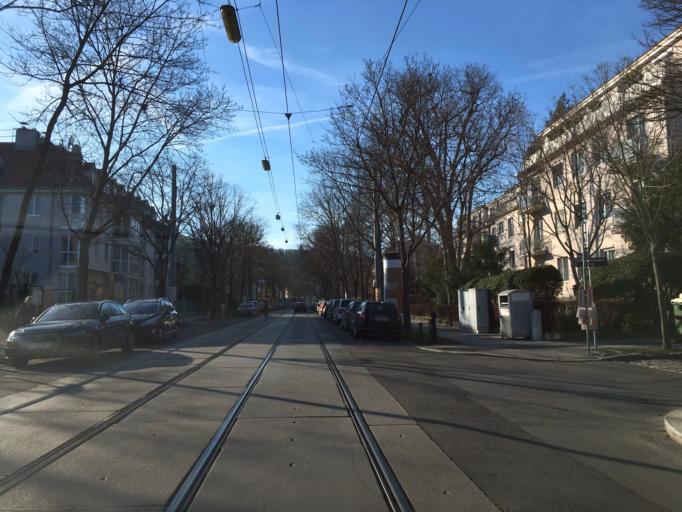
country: AT
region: Vienna
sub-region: Wien Stadt
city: Vienna
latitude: 48.2301
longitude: 16.2987
